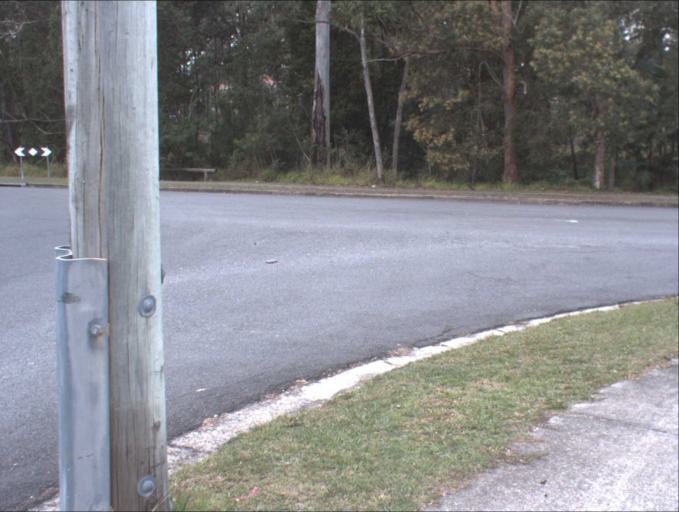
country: AU
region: Queensland
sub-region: Brisbane
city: Sunnybank Hills
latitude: -27.6568
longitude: 153.0429
